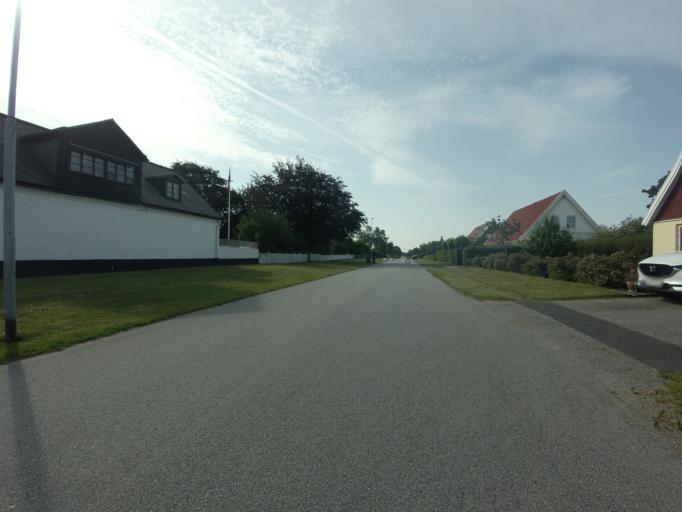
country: SE
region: Skane
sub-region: Malmo
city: Tygelsjo
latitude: 55.4954
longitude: 13.0105
